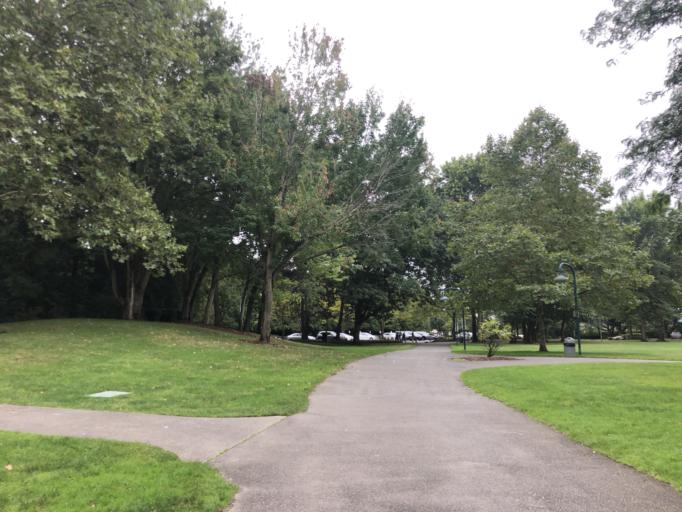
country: US
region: Washington
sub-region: King County
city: Renton
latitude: 47.5045
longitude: -122.2020
